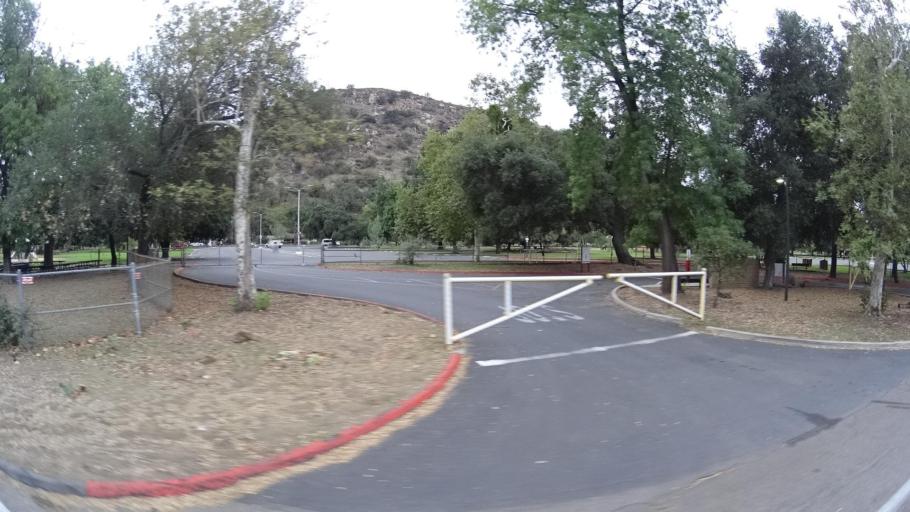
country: US
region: California
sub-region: San Diego County
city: Harbison Canyon
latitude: 32.8923
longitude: -116.8468
